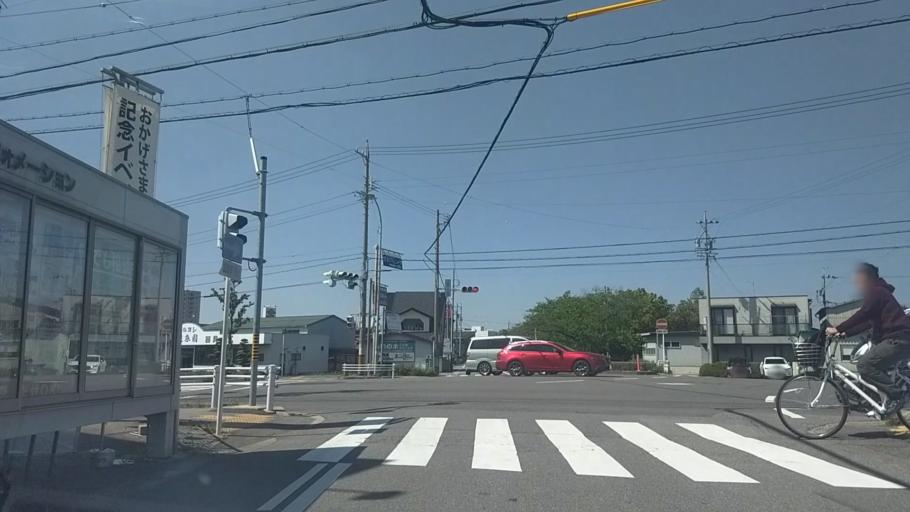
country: JP
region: Aichi
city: Okazaki
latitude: 34.9812
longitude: 137.1579
